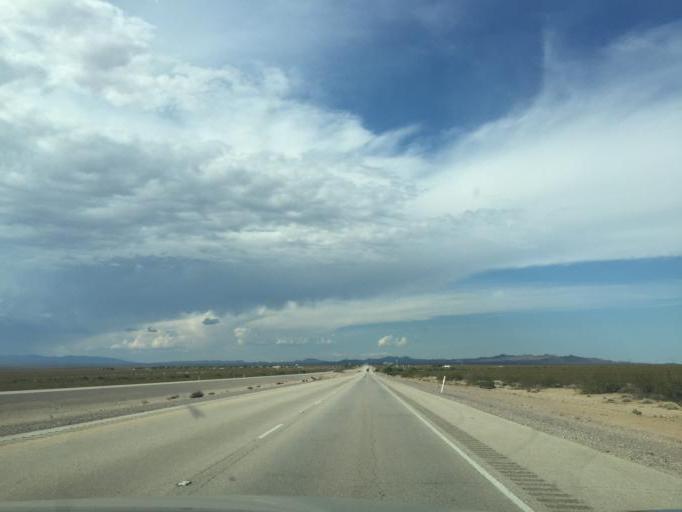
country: US
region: Nevada
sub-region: Clark County
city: Laughlin
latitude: 35.2812
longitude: -114.8744
